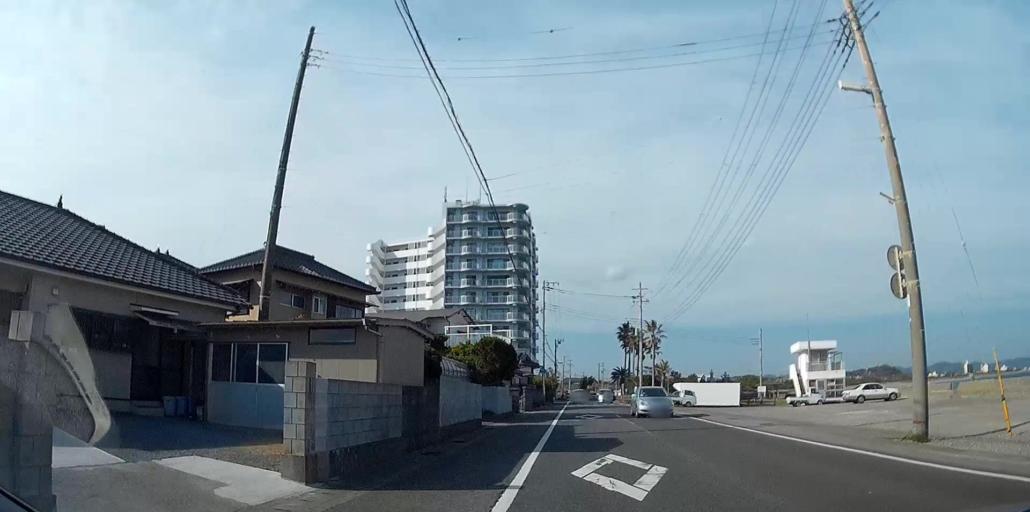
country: JP
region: Chiba
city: Tateyama
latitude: 34.9626
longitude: 139.9604
